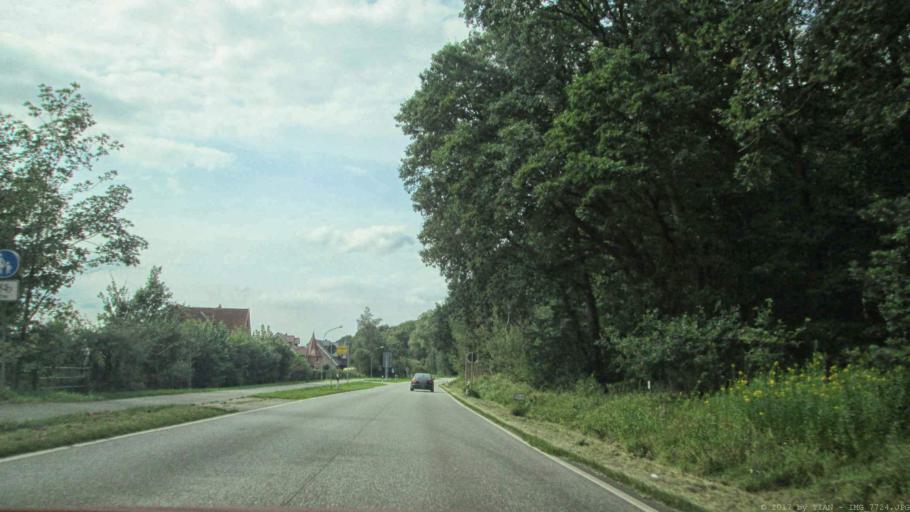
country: DE
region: Schleswig-Holstein
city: Escheburg
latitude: 53.4593
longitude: 10.3335
